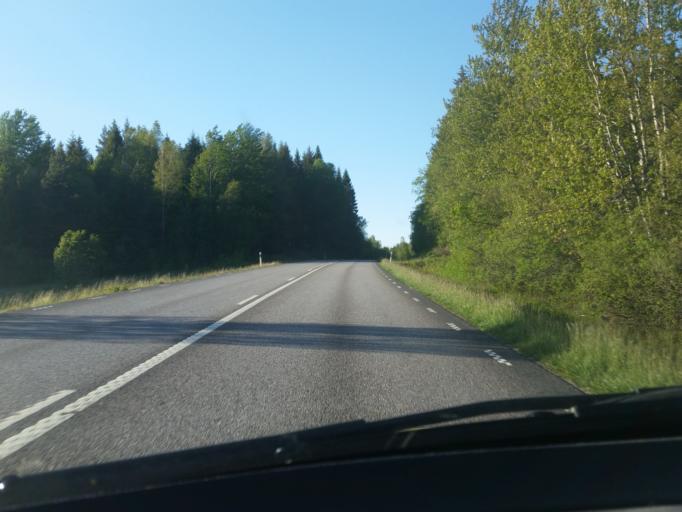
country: SE
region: Vaestra Goetaland
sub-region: Fargelanda Kommun
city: Faergelanda
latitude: 58.5246
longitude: 11.9783
